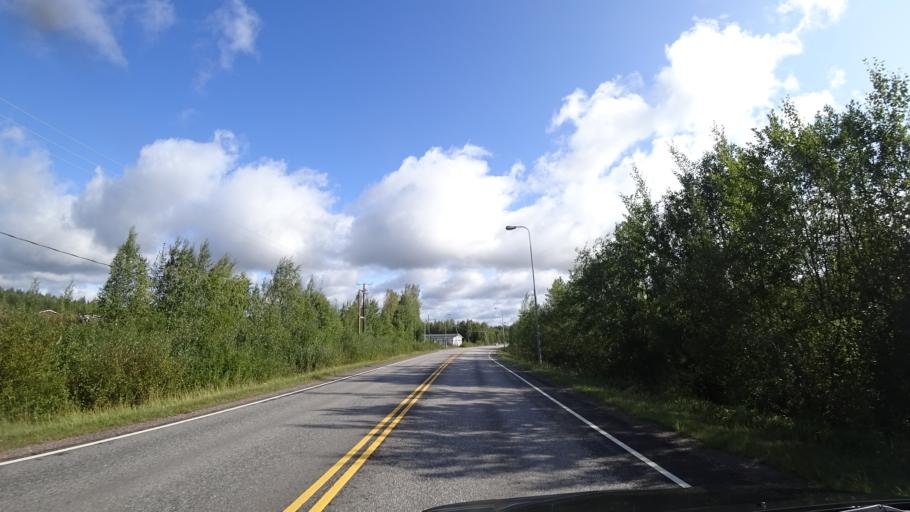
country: FI
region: Uusimaa
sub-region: Helsinki
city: Hyvinge
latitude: 60.5484
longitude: 24.9415
